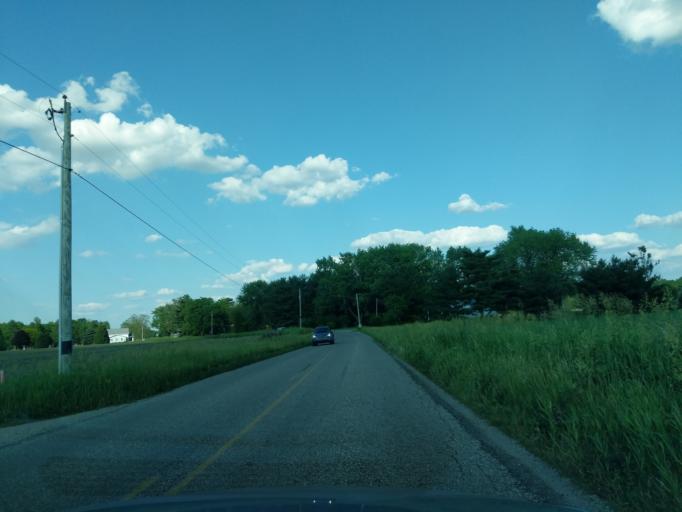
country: US
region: Indiana
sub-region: Kosciusko County
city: North Webster
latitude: 41.3057
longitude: -85.6403
